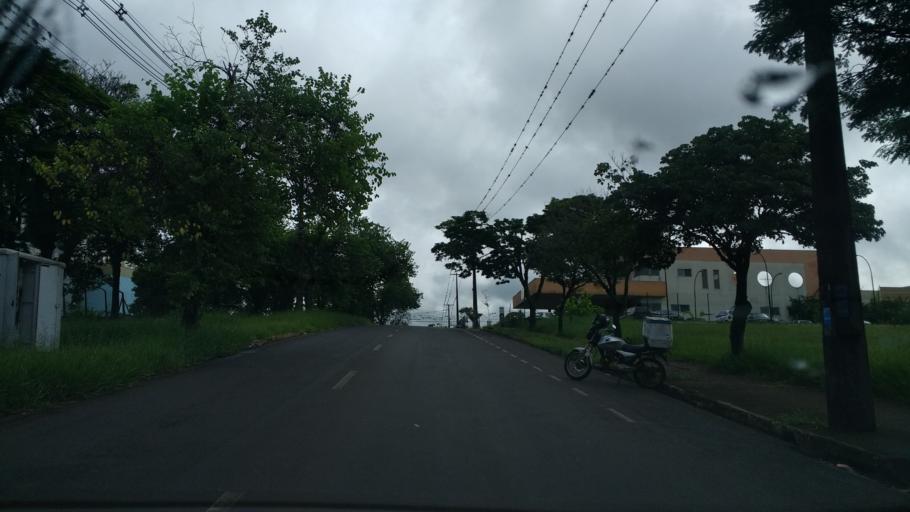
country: BR
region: Parana
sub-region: Londrina
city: Londrina
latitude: -23.3147
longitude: -51.2089
